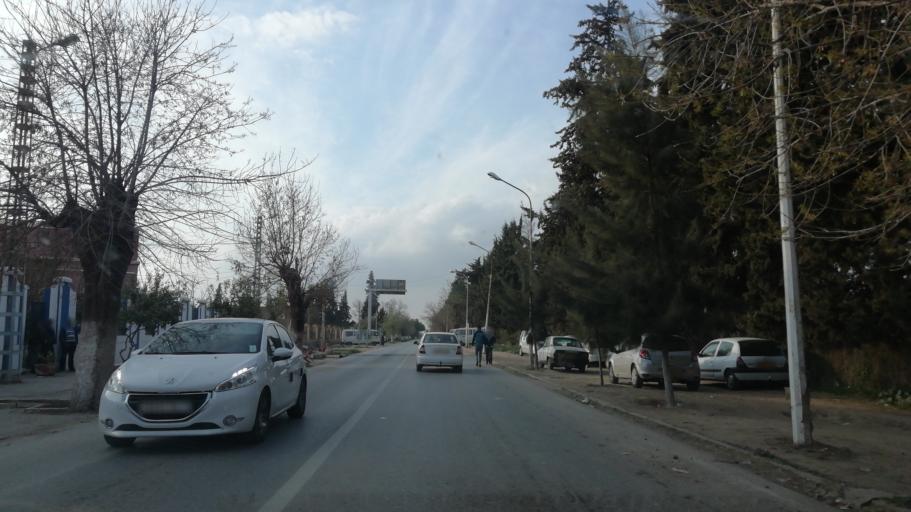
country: DZ
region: Mascara
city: Mascara
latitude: 35.5949
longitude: 0.0630
